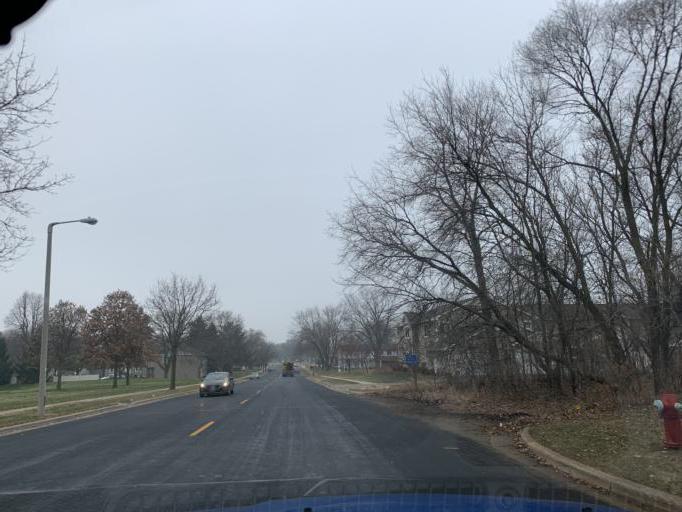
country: US
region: Wisconsin
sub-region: Dane County
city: Monona
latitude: 43.1017
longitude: -89.3131
